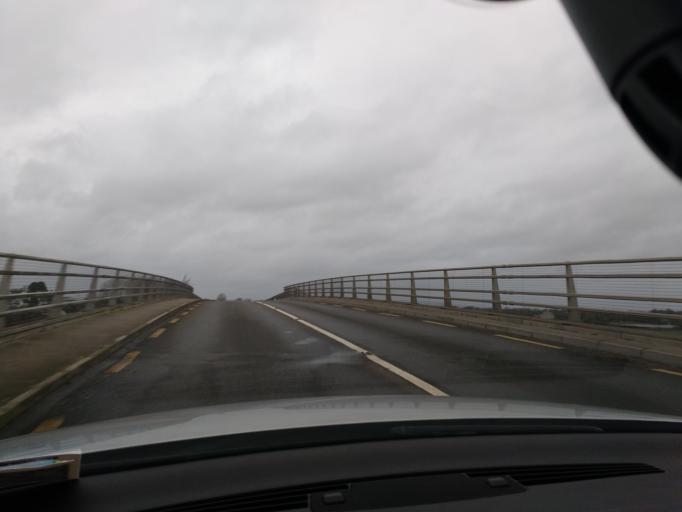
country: IE
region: Munster
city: Thurles
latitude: 52.6713
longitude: -7.6922
